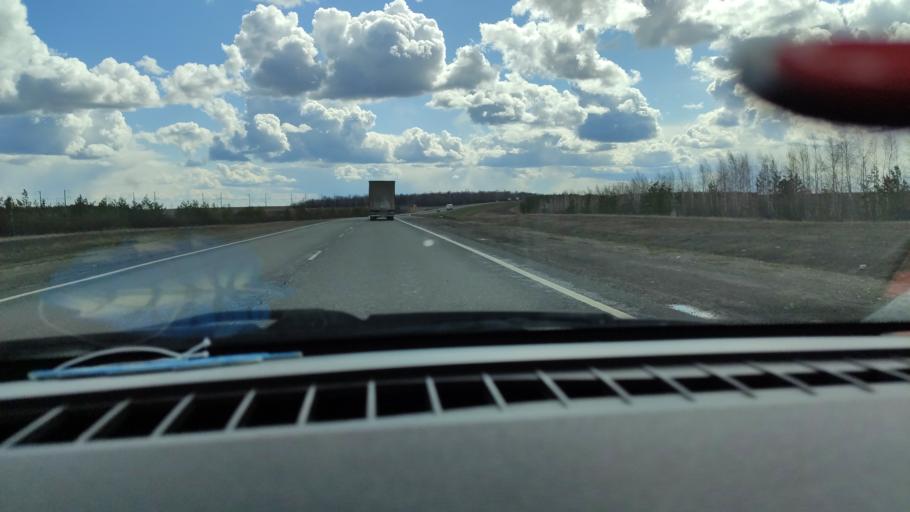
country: RU
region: Samara
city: Syzran'
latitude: 52.8740
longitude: 48.2881
